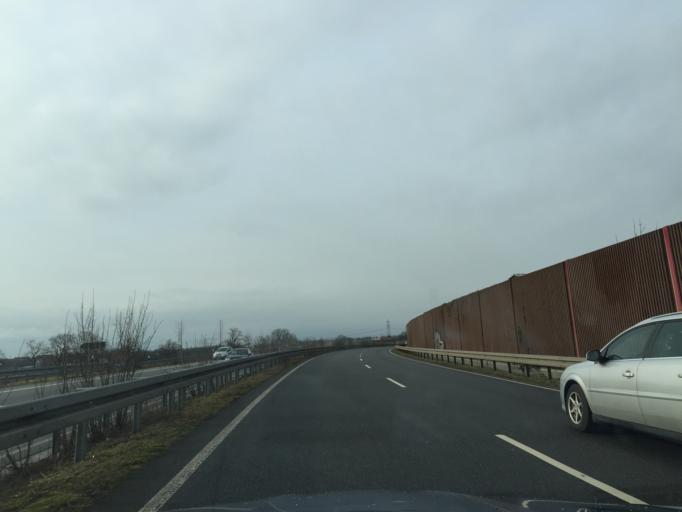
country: DE
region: Baden-Wuerttemberg
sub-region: Karlsruhe Region
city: Bruhl
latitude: 49.4004
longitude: 8.5571
